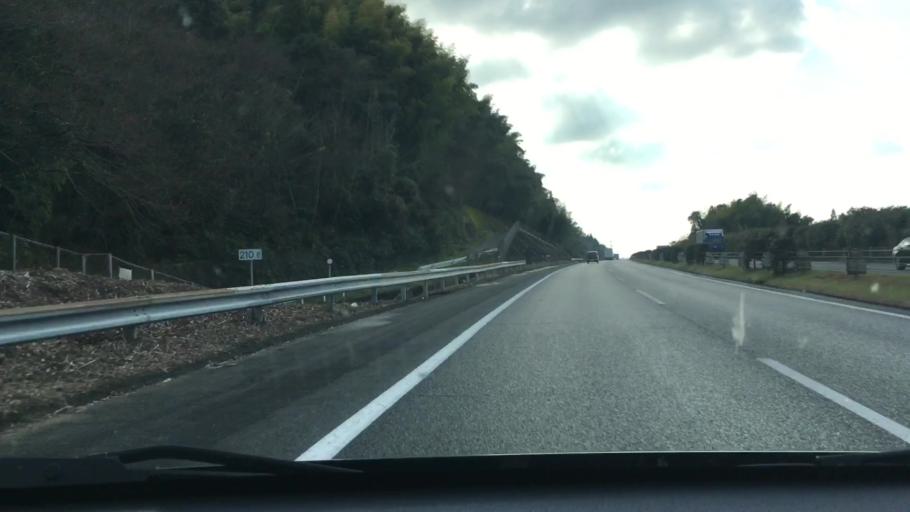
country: JP
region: Kumamoto
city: Yatsushiro
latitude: 32.5316
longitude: 130.6695
